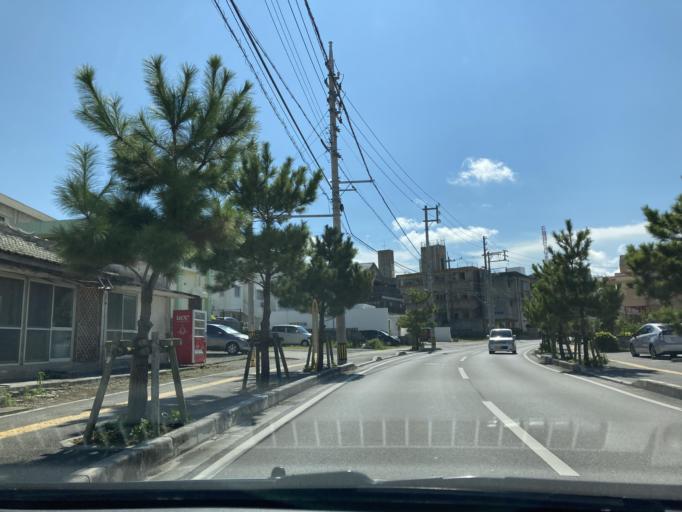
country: JP
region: Okinawa
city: Ginowan
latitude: 26.2208
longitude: 127.7322
